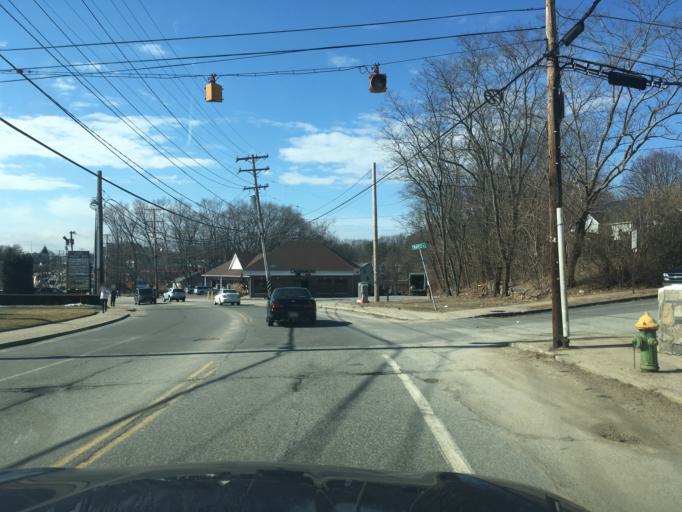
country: US
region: Rhode Island
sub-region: Providence County
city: Cranston
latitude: 41.7846
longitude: -71.4539
